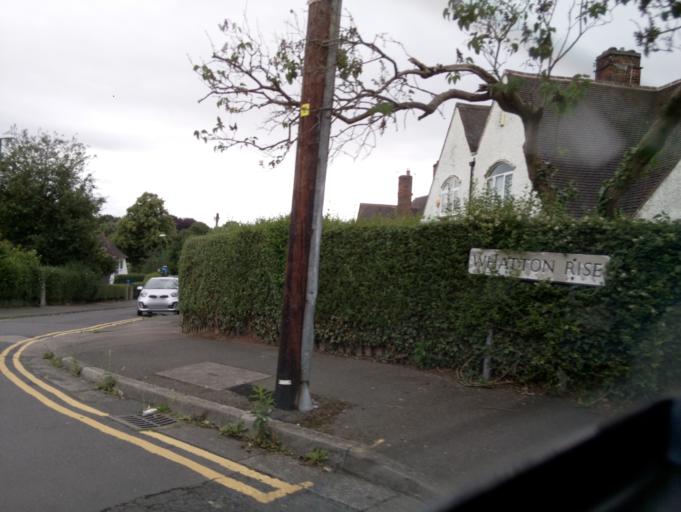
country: GB
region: England
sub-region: Nottinghamshire
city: Arnold
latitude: 52.9873
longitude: -1.1515
